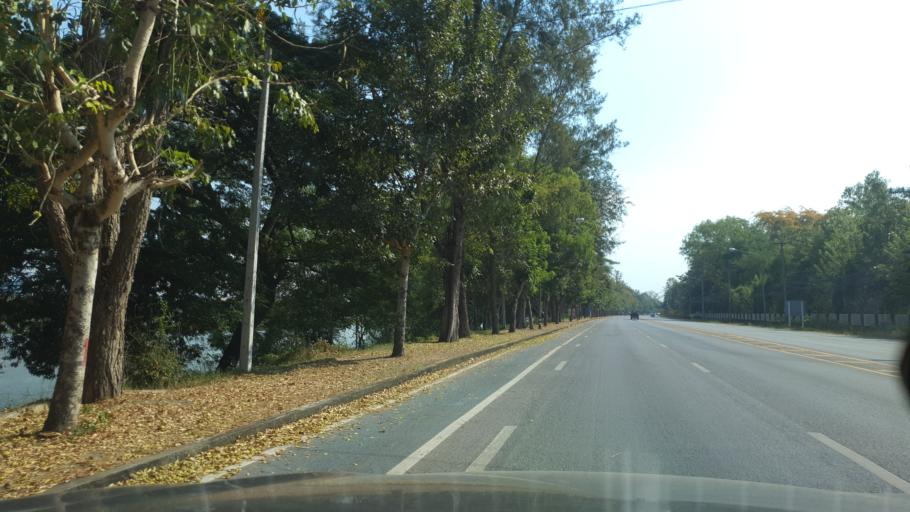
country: TH
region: Tak
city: Tak
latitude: 16.8747
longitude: 99.1173
